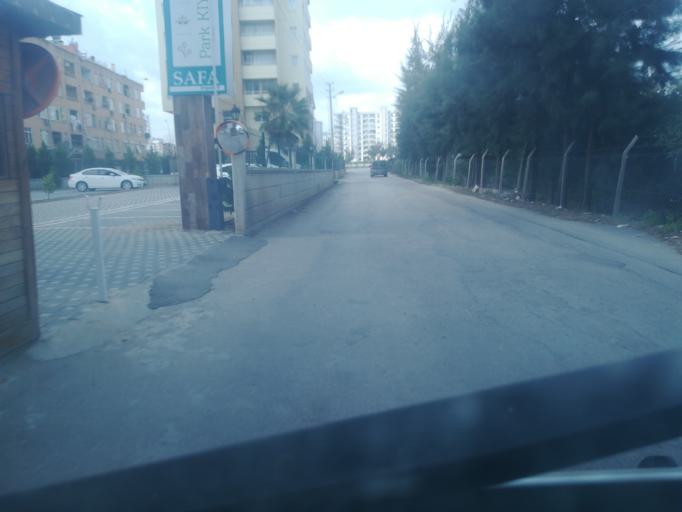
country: TR
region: Adana
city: Seyhan
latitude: 37.0078
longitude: 35.2701
